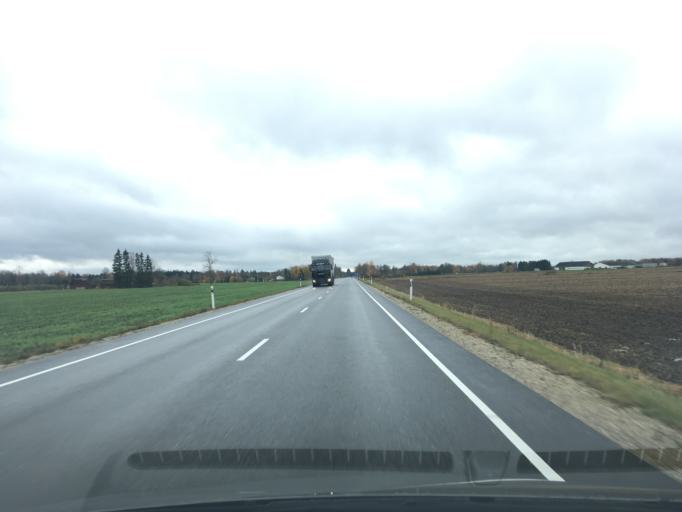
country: EE
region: Jogevamaa
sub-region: Tabivere vald
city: Tabivere
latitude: 58.4366
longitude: 26.4954
